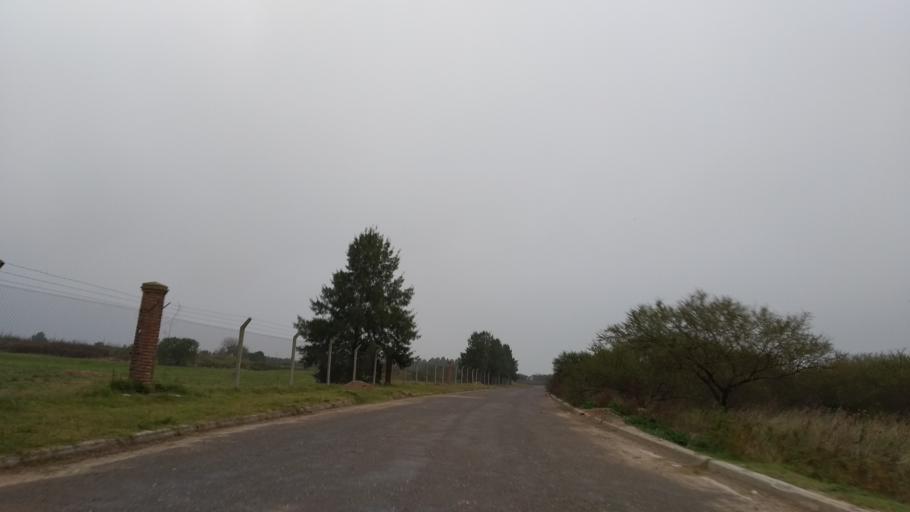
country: AR
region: Santa Fe
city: Funes
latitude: -32.9379
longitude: -60.7685
